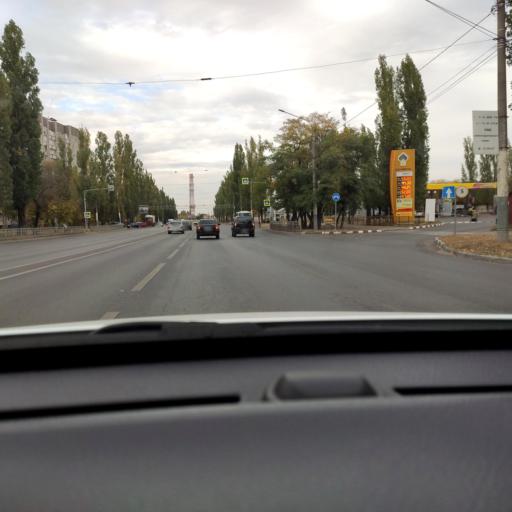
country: RU
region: Voronezj
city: Voronezh
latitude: 51.7037
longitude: 39.2755
